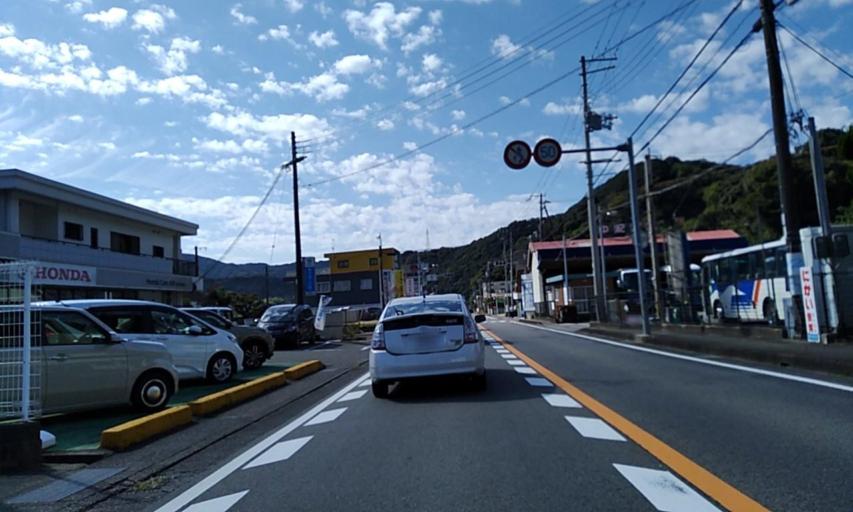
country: JP
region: Wakayama
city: Gobo
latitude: 33.9688
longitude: 135.1271
